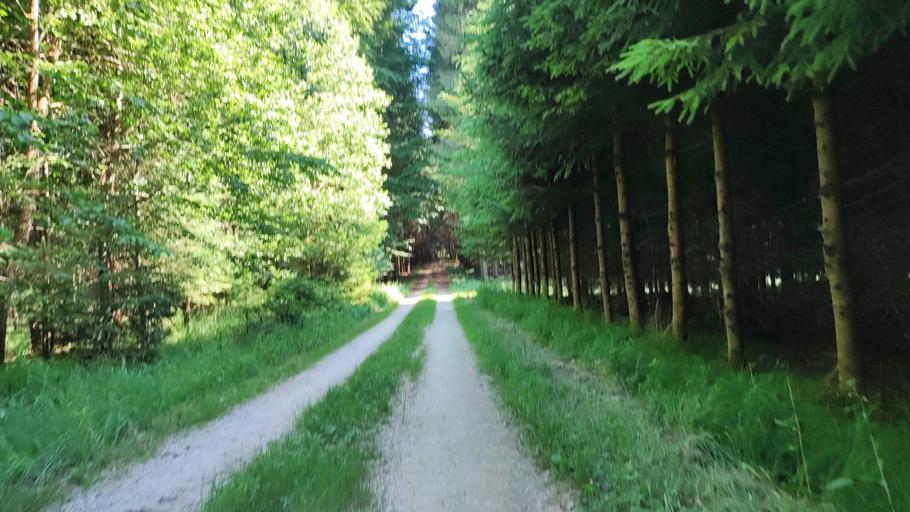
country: DE
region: Bavaria
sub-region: Swabia
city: Landensberg
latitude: 48.3708
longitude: 10.5105
